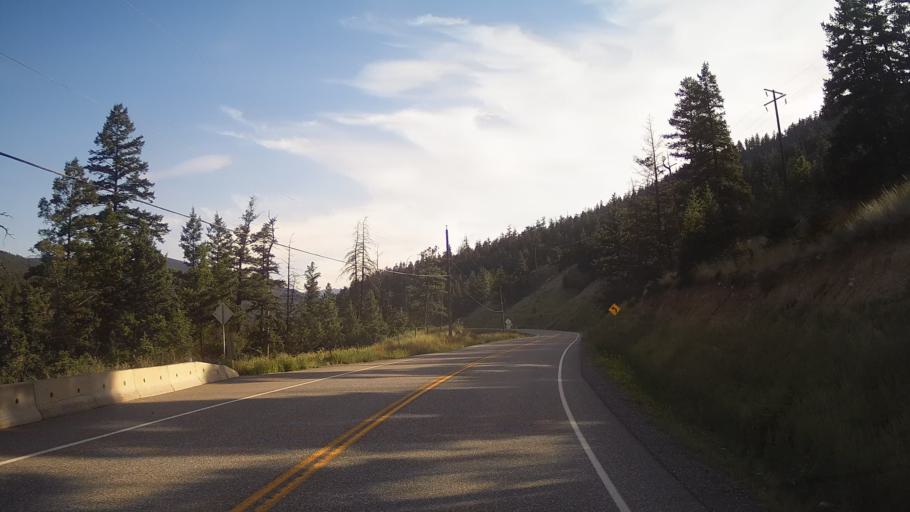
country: CA
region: British Columbia
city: Cache Creek
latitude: 50.8631
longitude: -121.5276
